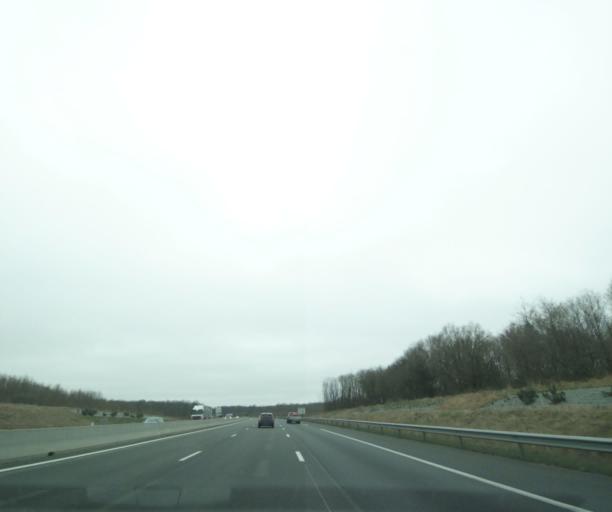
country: FR
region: Centre
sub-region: Departement du Cher
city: Vierzon
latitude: 47.2584
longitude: 2.0462
